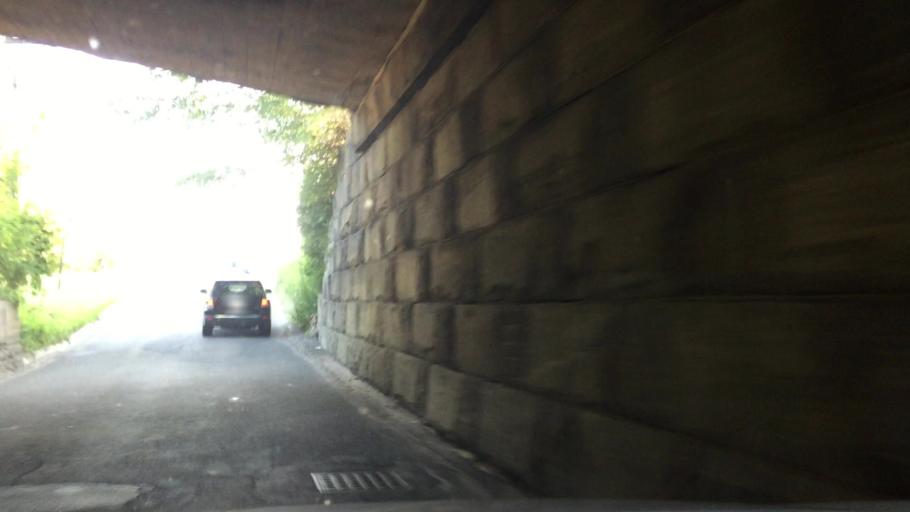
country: US
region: Massachusetts
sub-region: Berkshire County
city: Dalton
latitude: 42.4585
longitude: -73.1895
